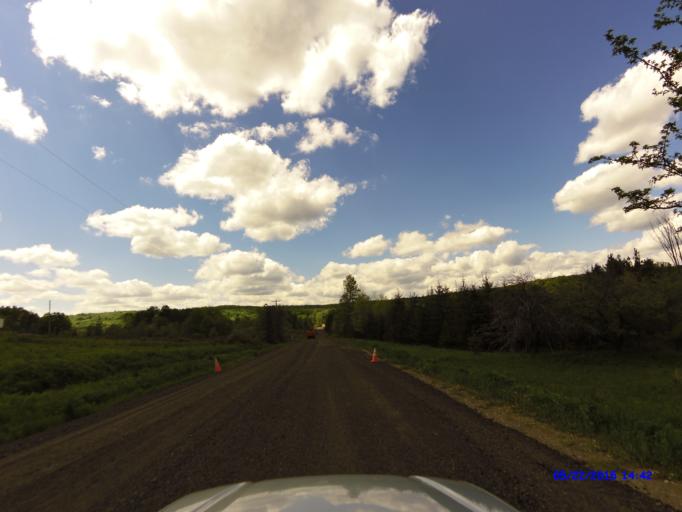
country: US
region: New York
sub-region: Cattaraugus County
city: Franklinville
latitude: 42.3525
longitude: -78.5579
